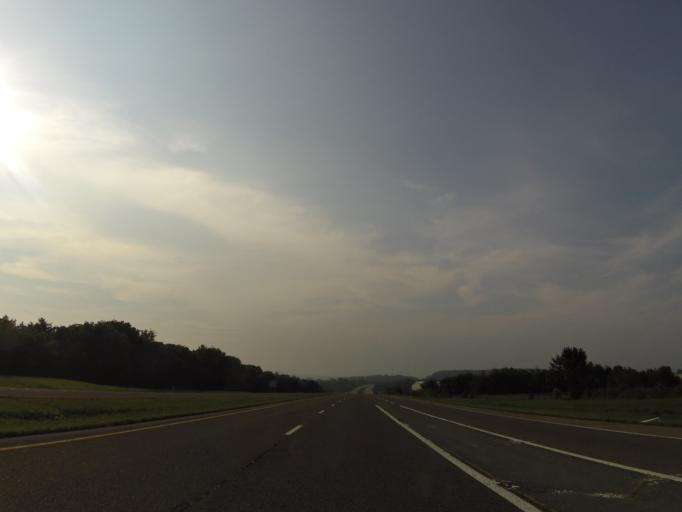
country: US
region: Tennessee
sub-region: Blount County
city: Alcoa
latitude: 35.8334
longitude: -83.9664
